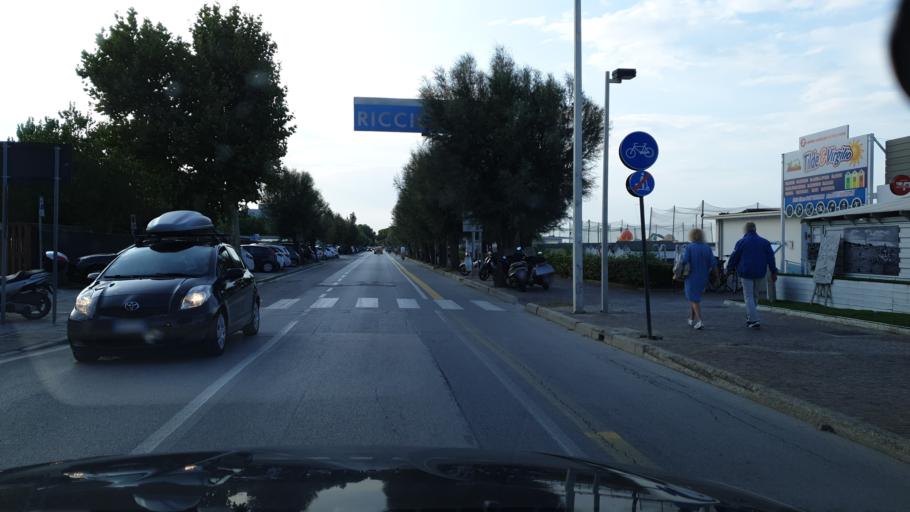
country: IT
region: Emilia-Romagna
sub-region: Provincia di Rimini
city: Misano Adriatico
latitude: 43.9857
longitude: 12.6888
